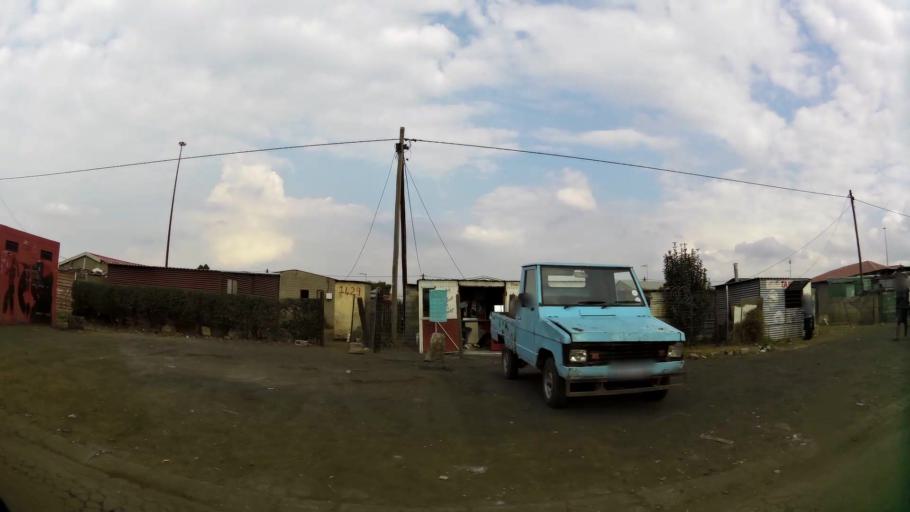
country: ZA
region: Gauteng
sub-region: Sedibeng District Municipality
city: Vanderbijlpark
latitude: -26.6742
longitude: 27.8730
